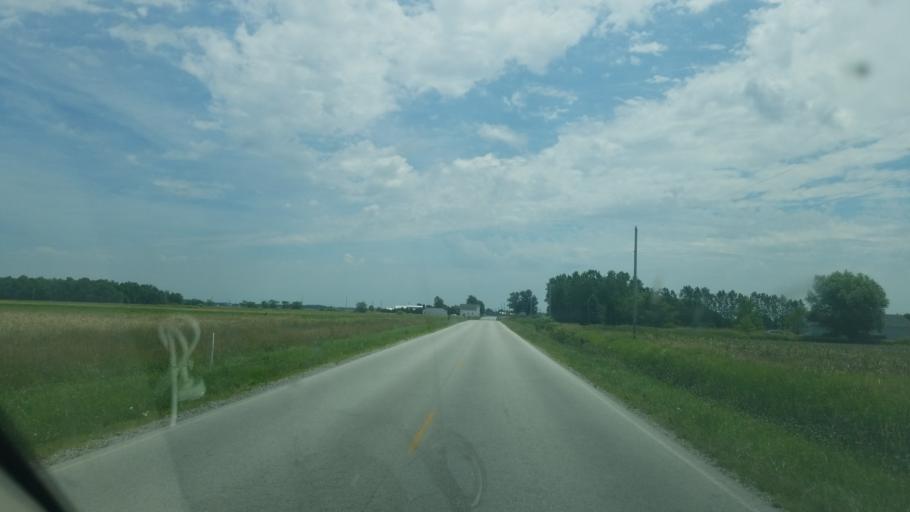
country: US
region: Ohio
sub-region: Wood County
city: Bowling Green
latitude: 41.2968
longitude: -83.5989
